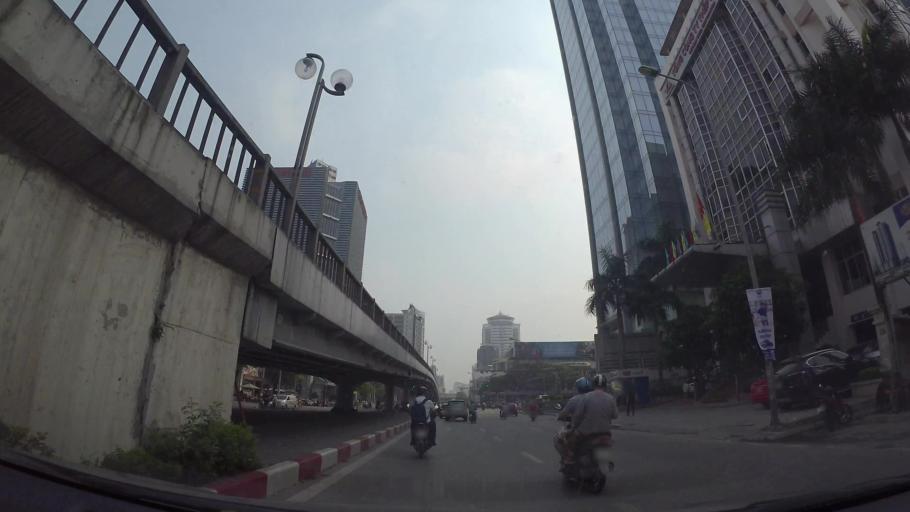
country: VN
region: Ha Noi
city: Dong Da
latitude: 21.0158
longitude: 105.8145
